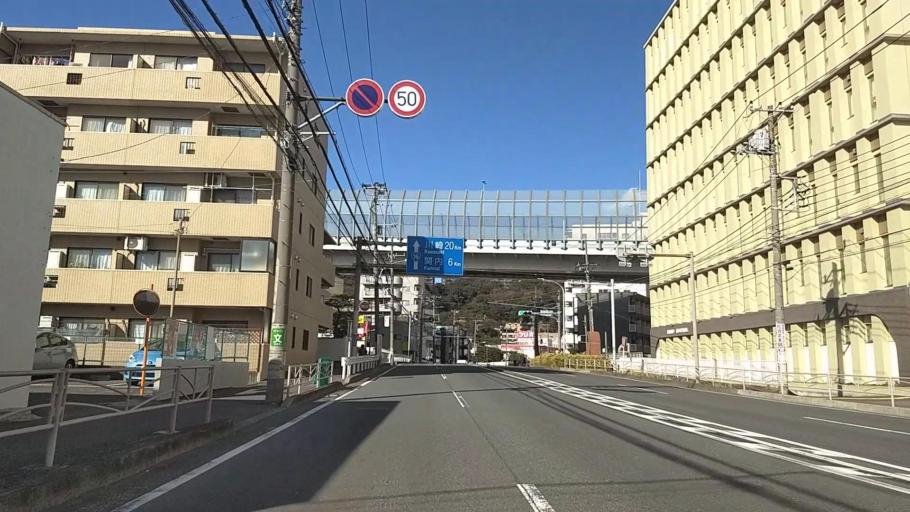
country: JP
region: Kanagawa
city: Yokohama
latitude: 35.3960
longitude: 139.6142
